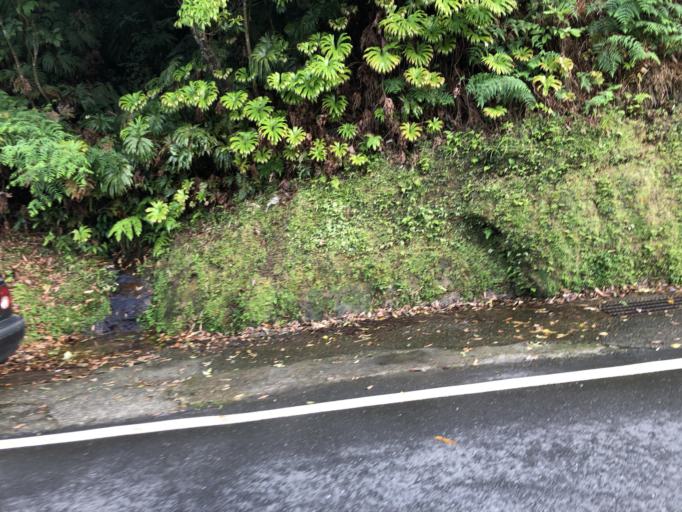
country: TW
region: Taiwan
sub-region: Keelung
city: Keelung
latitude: 25.1489
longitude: 121.6188
